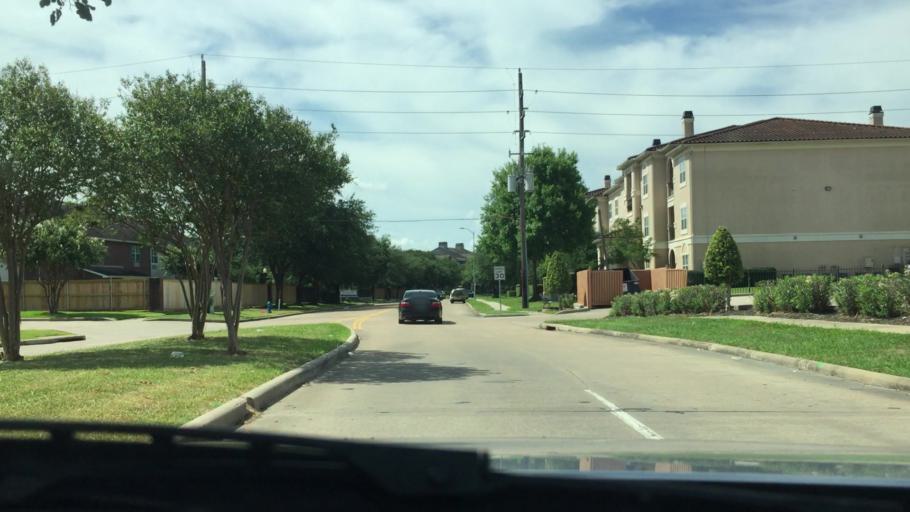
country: US
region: Texas
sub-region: Harris County
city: Bunker Hill Village
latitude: 29.7359
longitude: -95.5982
